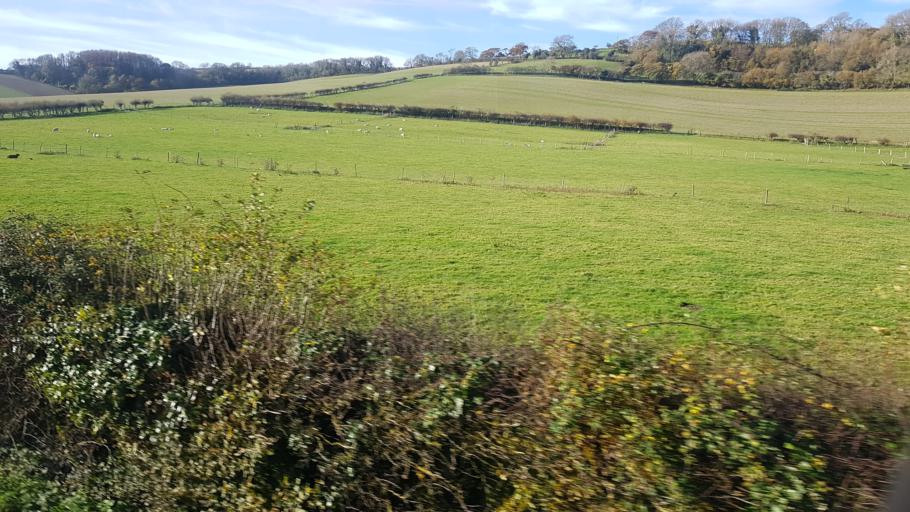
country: GB
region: England
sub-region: Isle of Wight
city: Newport
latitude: 50.6726
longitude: -1.3426
